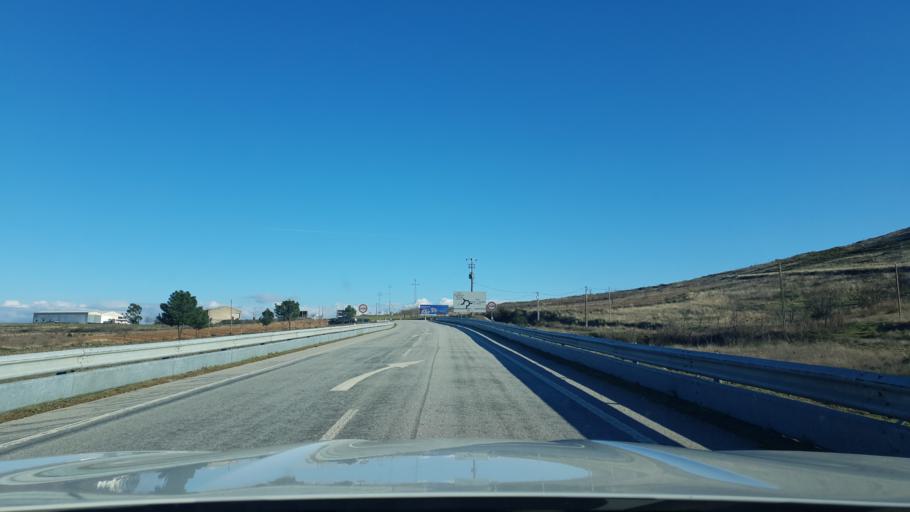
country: PT
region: Braganca
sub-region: Freixo de Espada A Cinta
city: Freixo de Espada a Cinta
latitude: 41.1782
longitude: -6.7957
